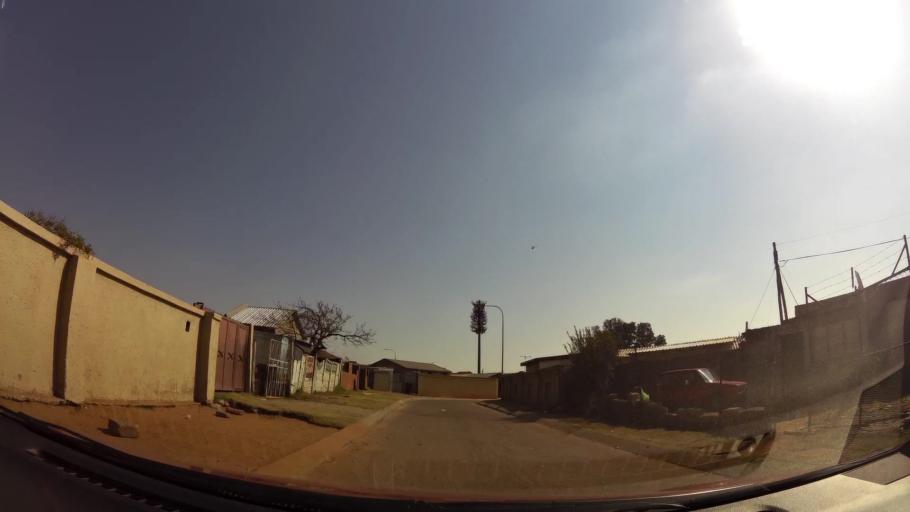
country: ZA
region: Gauteng
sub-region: City of Johannesburg Metropolitan Municipality
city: Johannesburg
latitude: -26.2438
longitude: 27.9606
